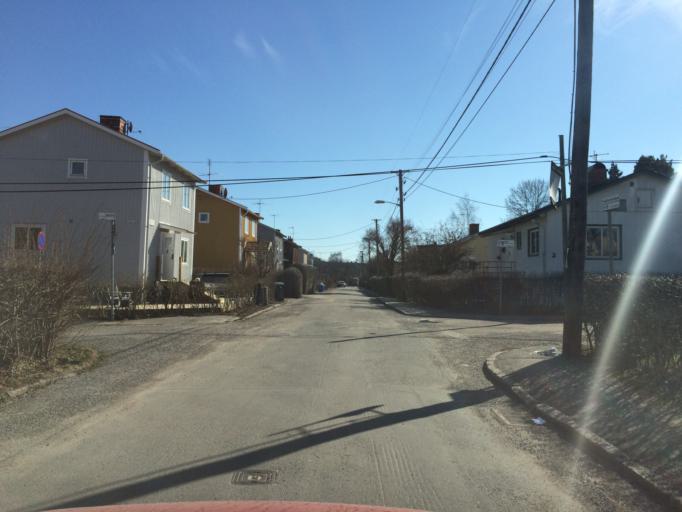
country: SE
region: Stockholm
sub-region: Huddinge Kommun
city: Huddinge
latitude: 59.2821
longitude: 17.9963
